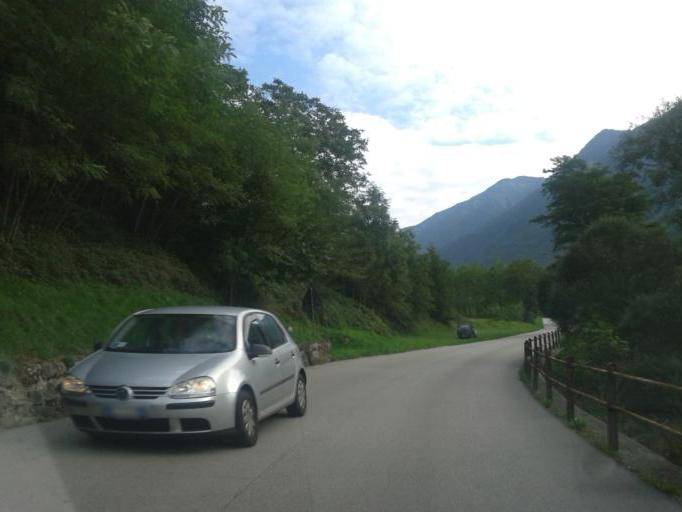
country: IT
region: Trentino-Alto Adige
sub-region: Provincia di Trento
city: Cimego
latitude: 45.9061
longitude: 10.6091
